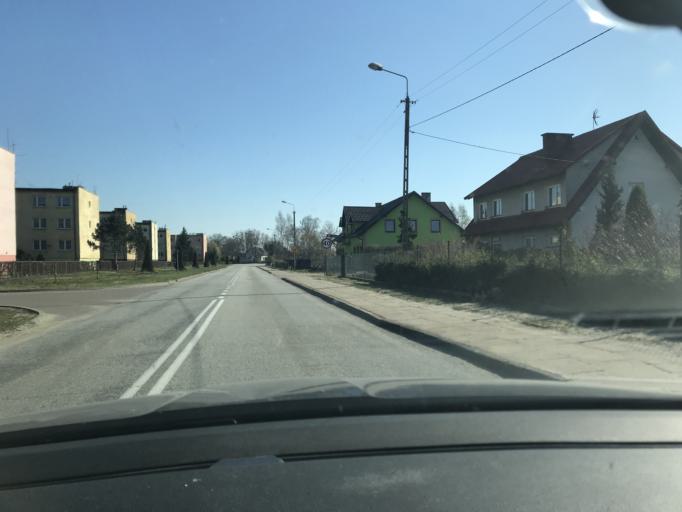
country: PL
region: Pomeranian Voivodeship
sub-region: Powiat nowodworski
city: Sztutowo
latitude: 54.3315
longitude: 19.1780
